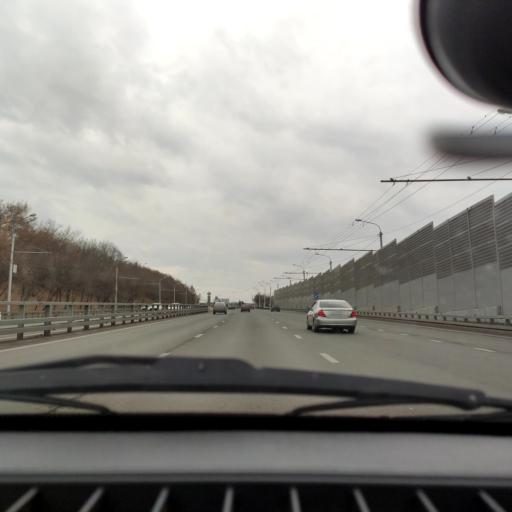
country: RU
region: Bashkortostan
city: Ufa
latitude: 54.7524
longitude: 55.9711
